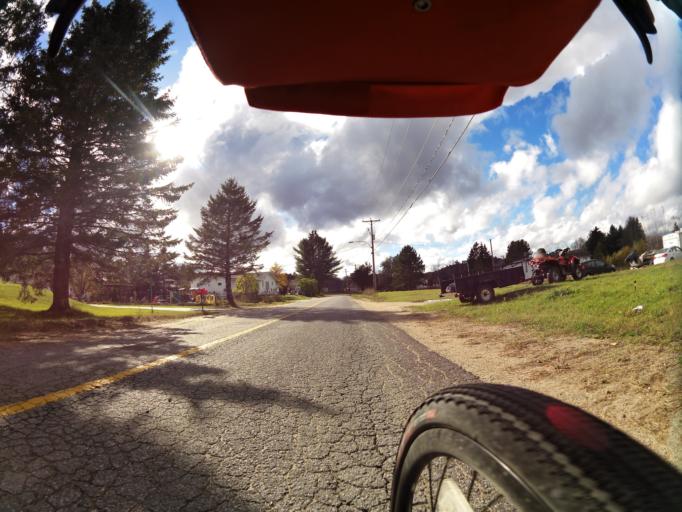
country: CA
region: Quebec
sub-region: Outaouais
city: Wakefield
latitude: 45.6868
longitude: -76.1195
